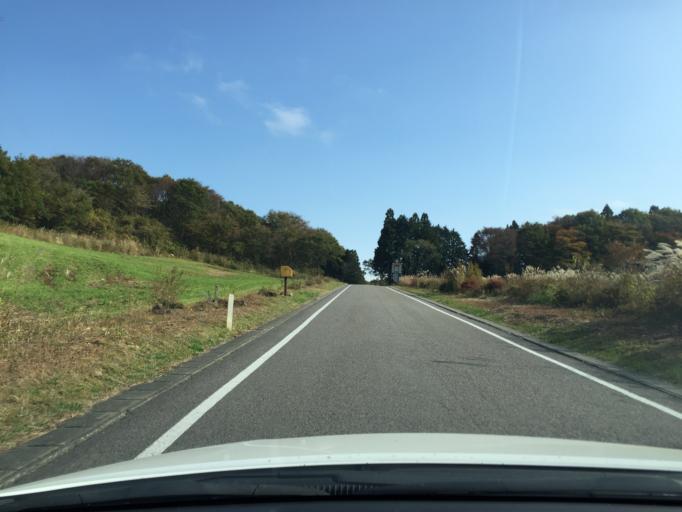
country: JP
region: Fukushima
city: Ishikawa
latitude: 36.9543
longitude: 140.5731
